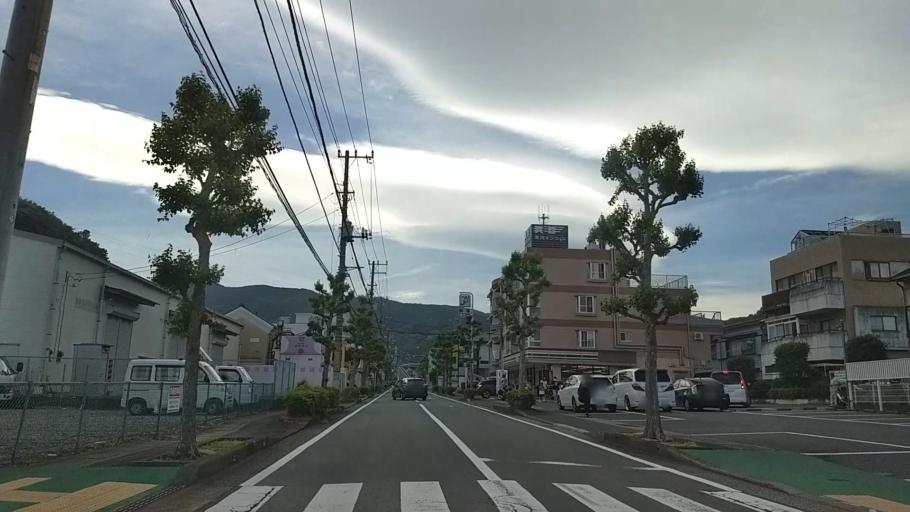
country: JP
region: Kanagawa
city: Odawara
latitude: 35.2440
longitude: 139.1384
